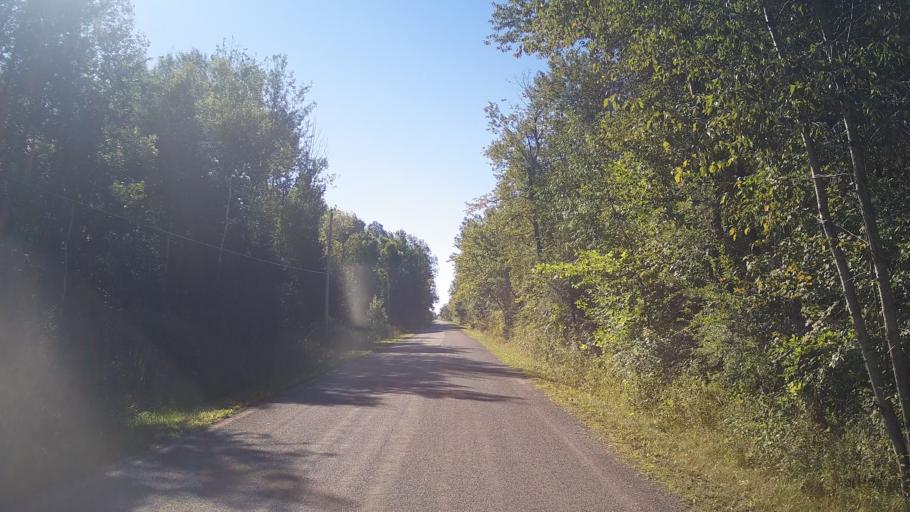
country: CA
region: Ontario
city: Prescott
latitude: 44.9833
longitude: -75.5801
